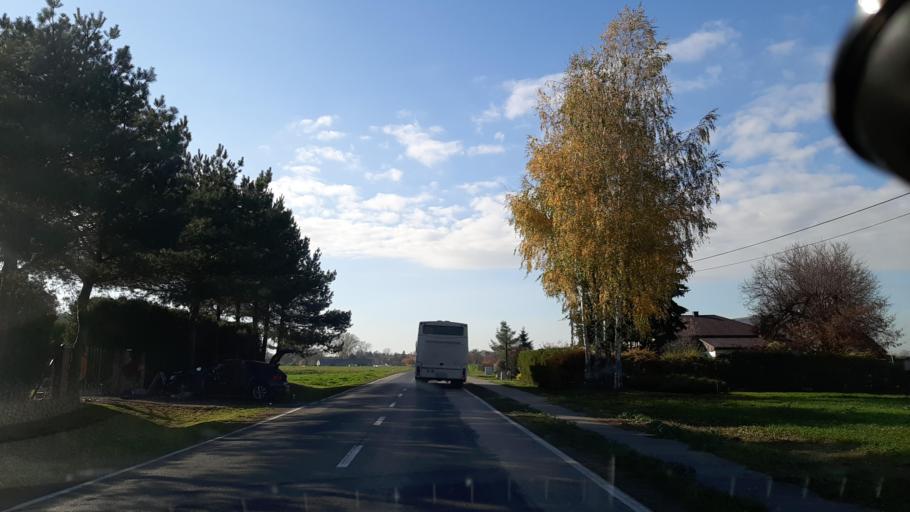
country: PL
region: Lublin Voivodeship
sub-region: Powiat lubelski
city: Jastkow
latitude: 51.3448
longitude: 22.4197
